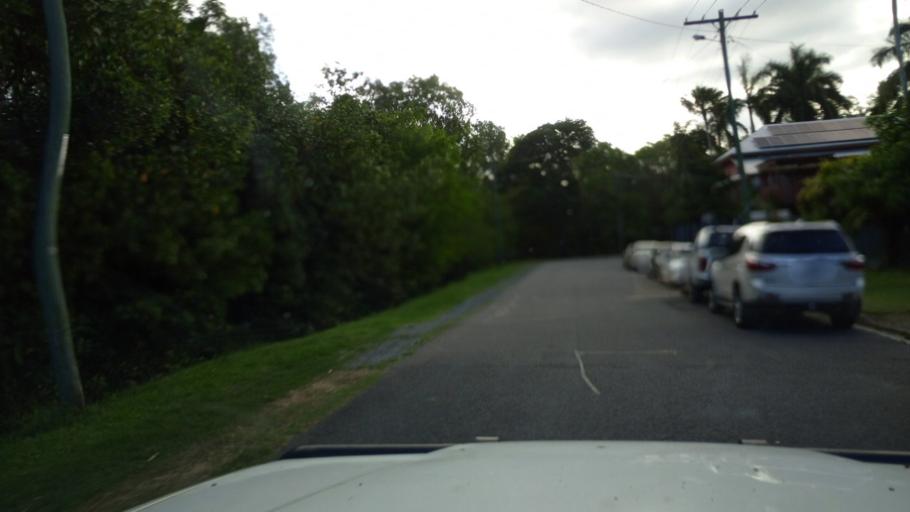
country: AU
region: Queensland
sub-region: Cairns
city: Cairns
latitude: -16.9172
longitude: 145.7560
